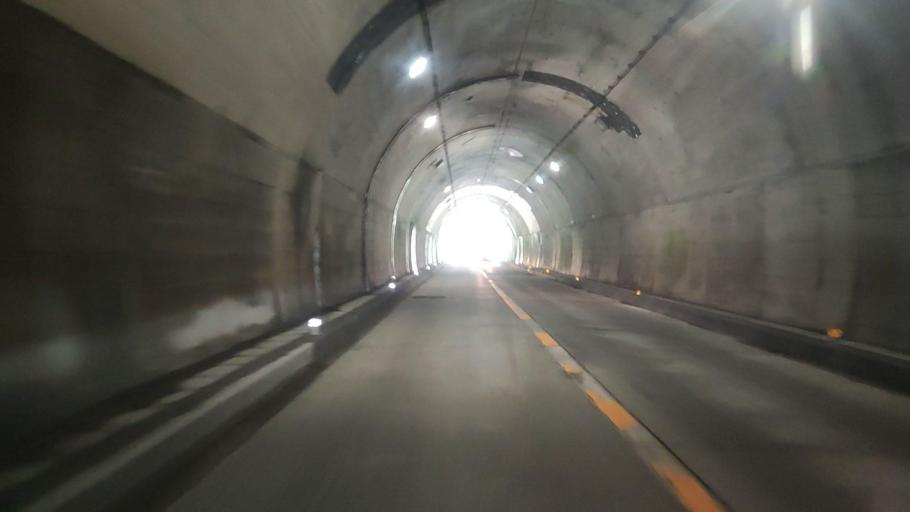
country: JP
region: Wakayama
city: Shingu
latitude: 33.8170
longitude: 135.8562
